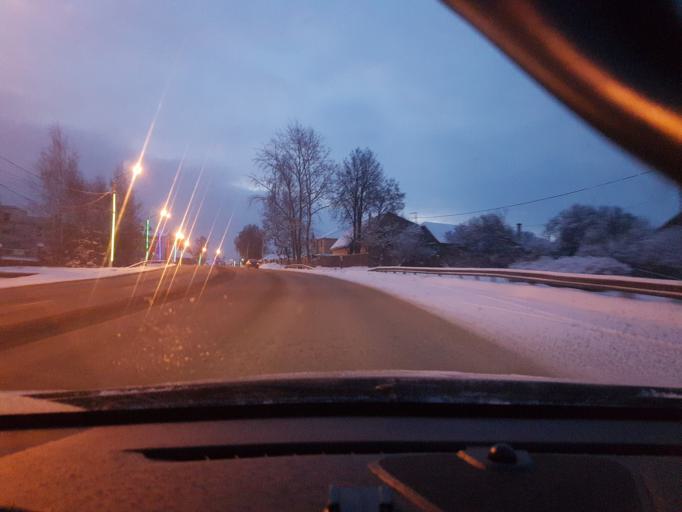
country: RU
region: Moskovskaya
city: Istra
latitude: 55.9090
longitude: 36.8766
